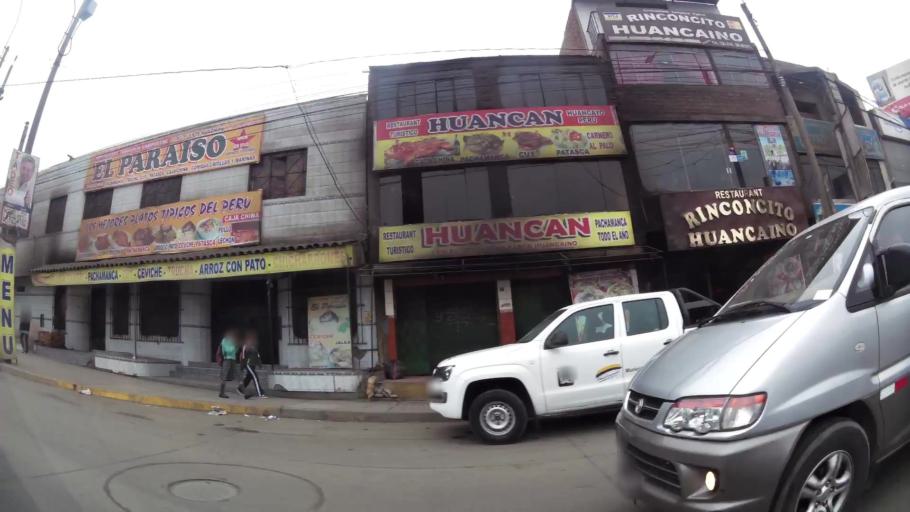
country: PE
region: Lima
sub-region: Lima
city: Santa Maria
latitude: -12.0160
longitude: -76.8989
